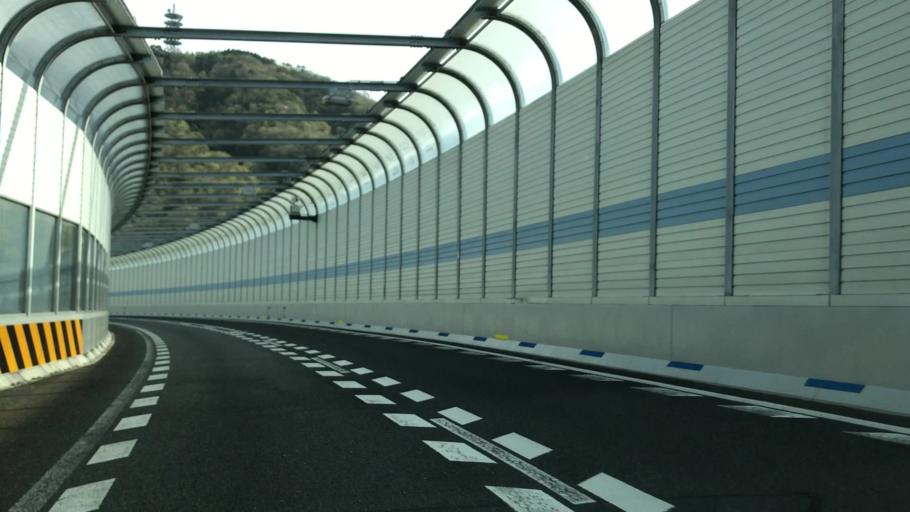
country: JP
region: Hyogo
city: Sandacho
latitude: 34.8219
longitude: 135.2610
